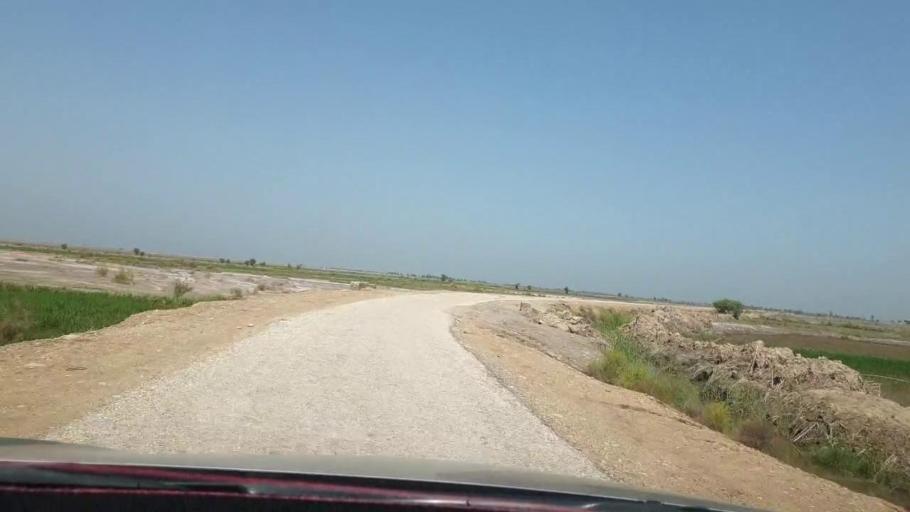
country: PK
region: Sindh
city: Warah
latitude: 27.5288
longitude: 67.7128
